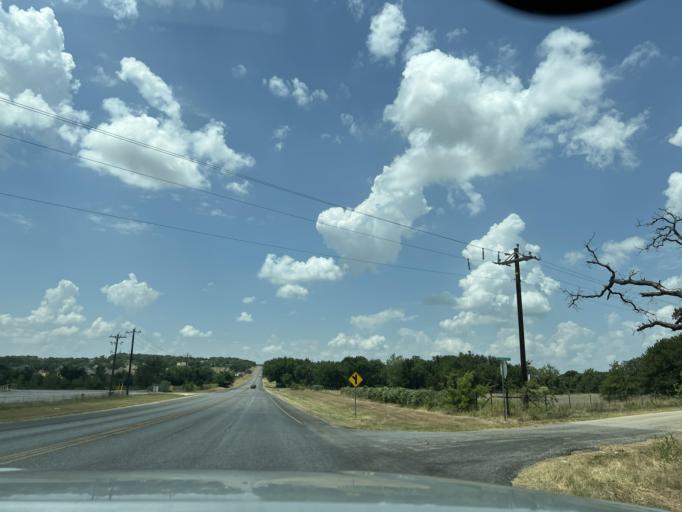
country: US
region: Texas
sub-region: Parker County
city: Springtown
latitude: 32.9431
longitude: -97.6940
